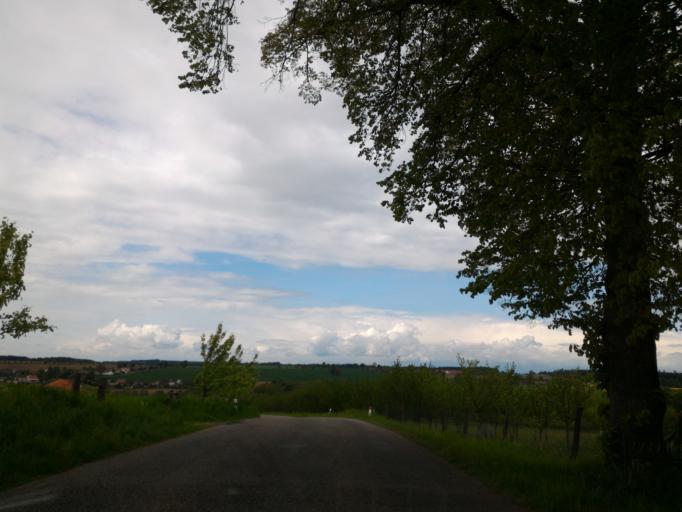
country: CZ
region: Central Bohemia
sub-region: Okres Kutna Hora
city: Zbraslavice
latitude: 49.7795
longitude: 15.2331
